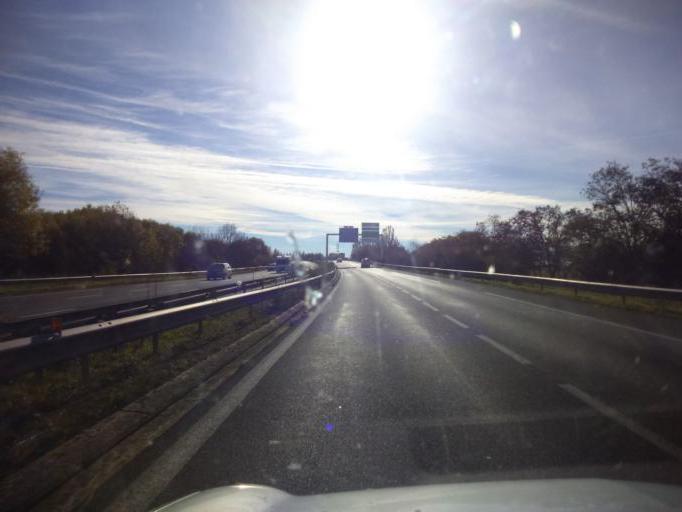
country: FR
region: Poitou-Charentes
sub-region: Departement de la Charente-Maritime
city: Breuil-Magne
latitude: 45.9711
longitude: -0.9853
